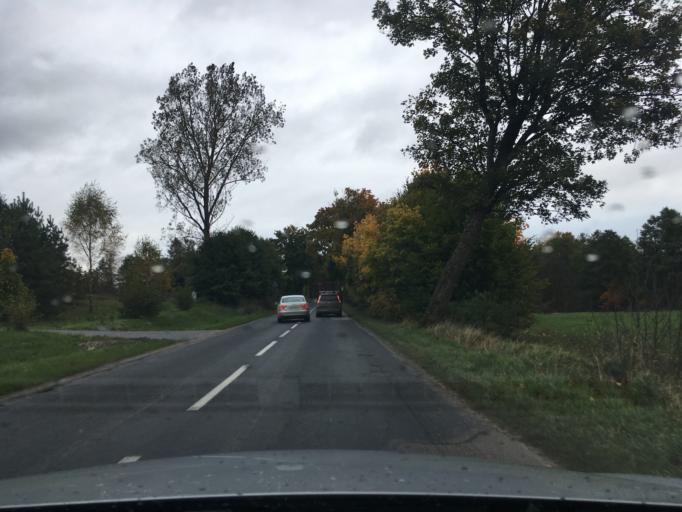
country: PL
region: Pomeranian Voivodeship
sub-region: Powiat koscierski
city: Liniewo
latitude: 54.1434
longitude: 18.2415
